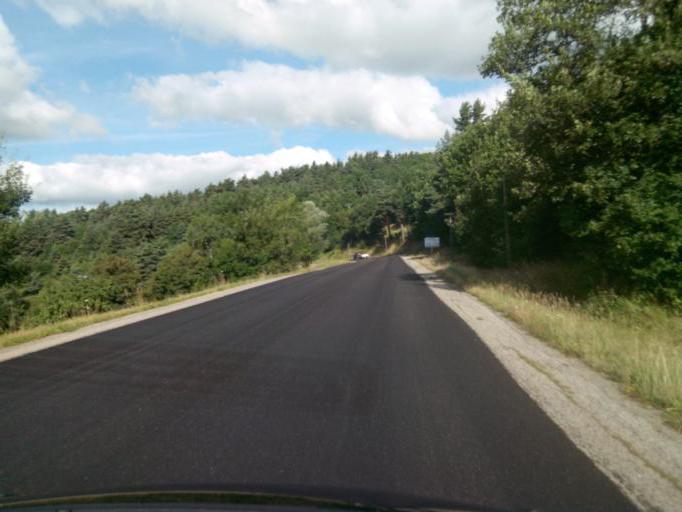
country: FR
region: Auvergne
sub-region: Departement de la Haute-Loire
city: Retournac
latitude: 45.2266
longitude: 4.0459
